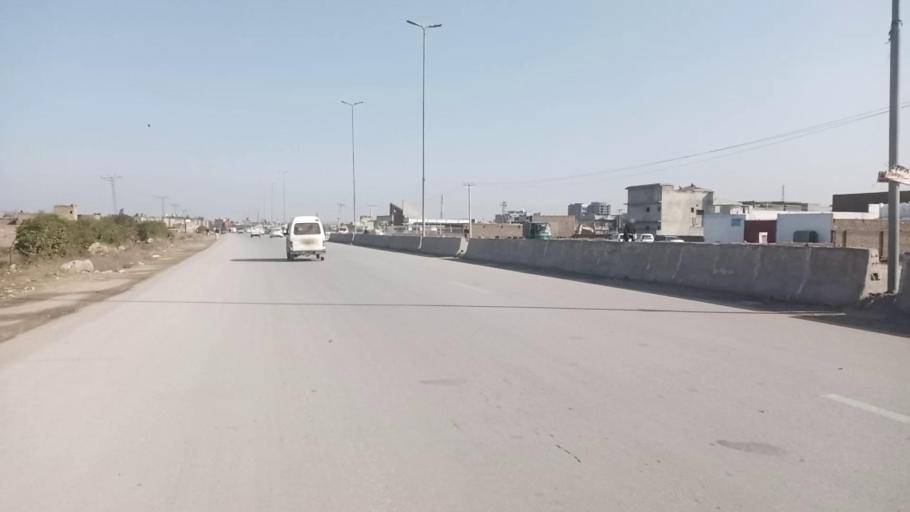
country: PK
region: Khyber Pakhtunkhwa
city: Peshawar
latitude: 34.0339
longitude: 71.5680
